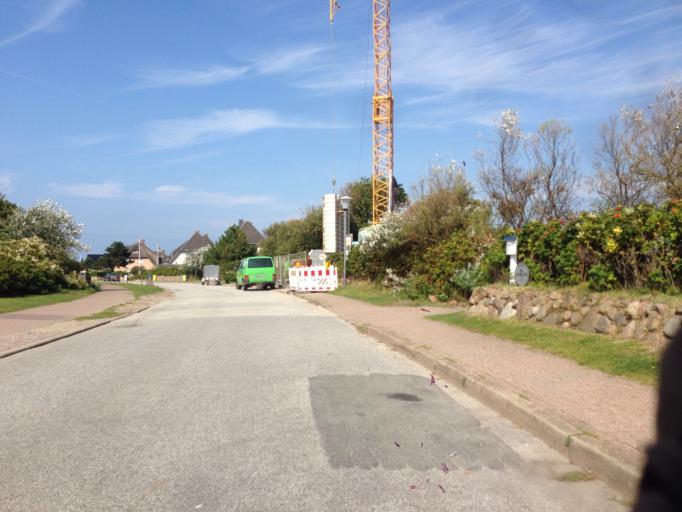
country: DE
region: Schleswig-Holstein
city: Westerland
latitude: 54.8484
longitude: 8.2946
